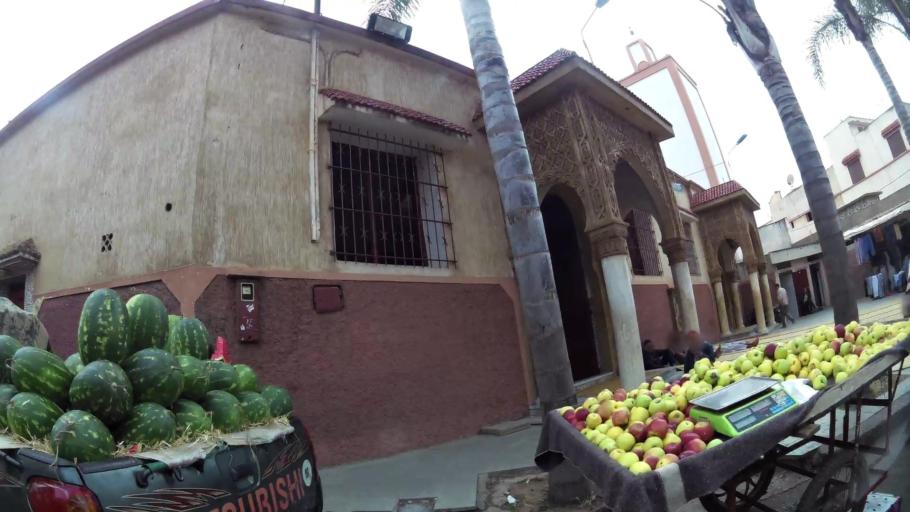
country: MA
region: Rabat-Sale-Zemmour-Zaer
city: Sale
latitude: 34.0433
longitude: -6.8075
